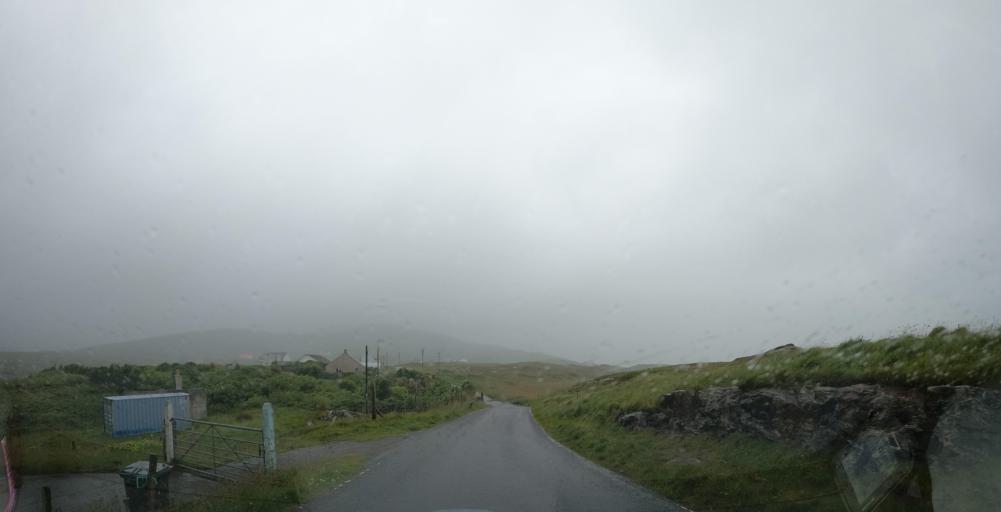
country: GB
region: Scotland
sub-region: Eilean Siar
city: Barra
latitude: 57.0086
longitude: -7.4165
